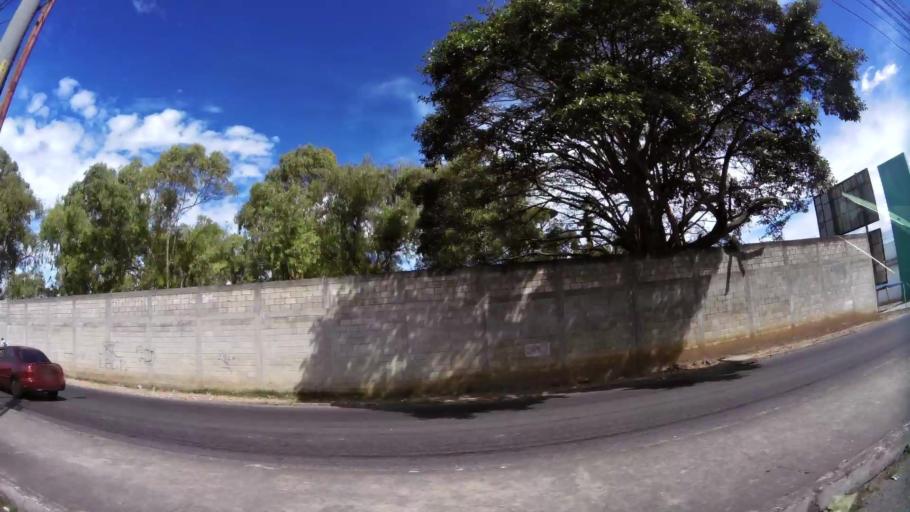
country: GT
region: Guatemala
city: Mixco
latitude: 14.6583
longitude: -90.5700
